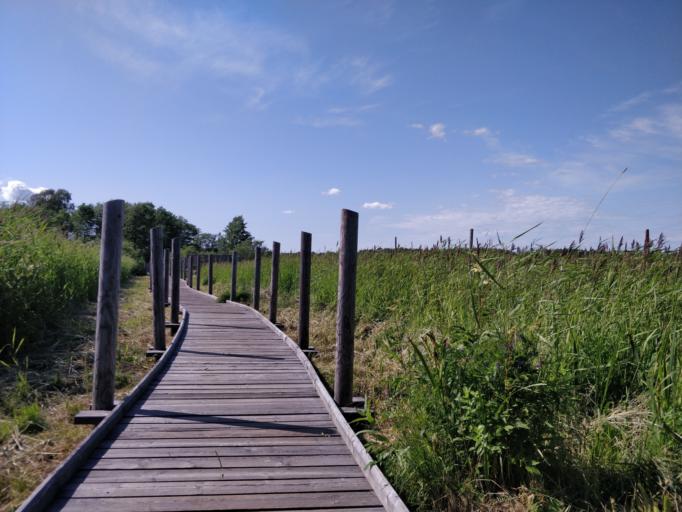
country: FI
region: Uusimaa
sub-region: Helsinki
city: Helsinki
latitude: 60.2086
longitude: 24.9962
